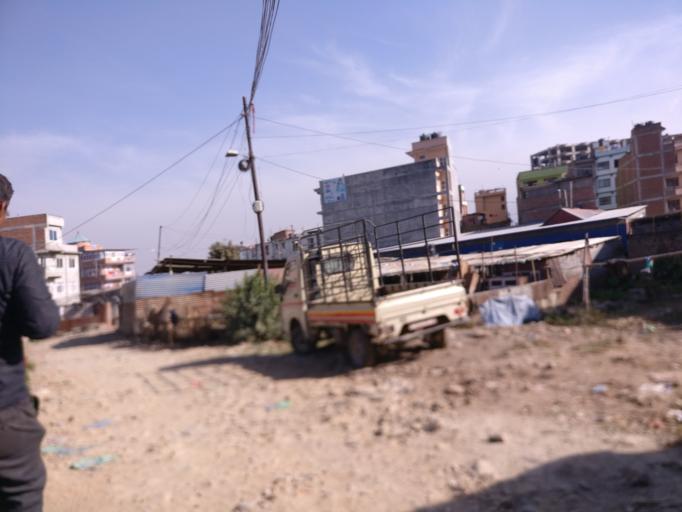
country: NP
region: Central Region
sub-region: Bagmati Zone
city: Patan
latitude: 27.6692
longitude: 85.3334
